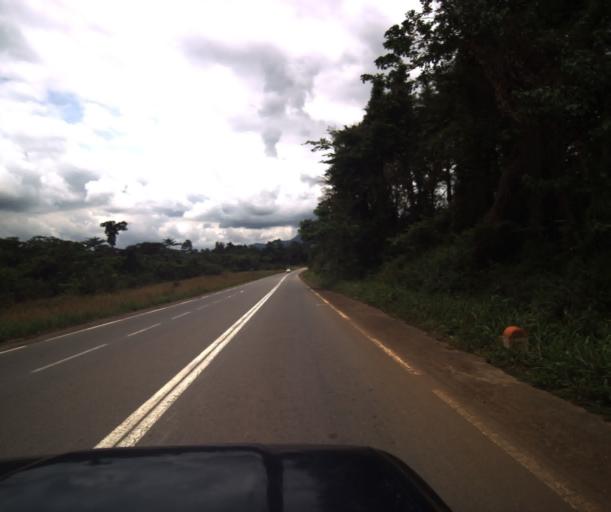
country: CM
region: Centre
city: Eseka
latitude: 3.8759
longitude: 10.8176
